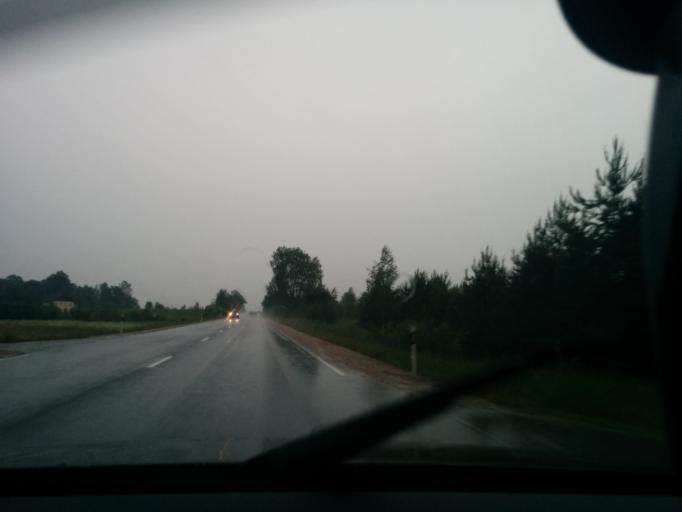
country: LV
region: Ikskile
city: Ikskile
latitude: 56.8728
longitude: 24.5365
